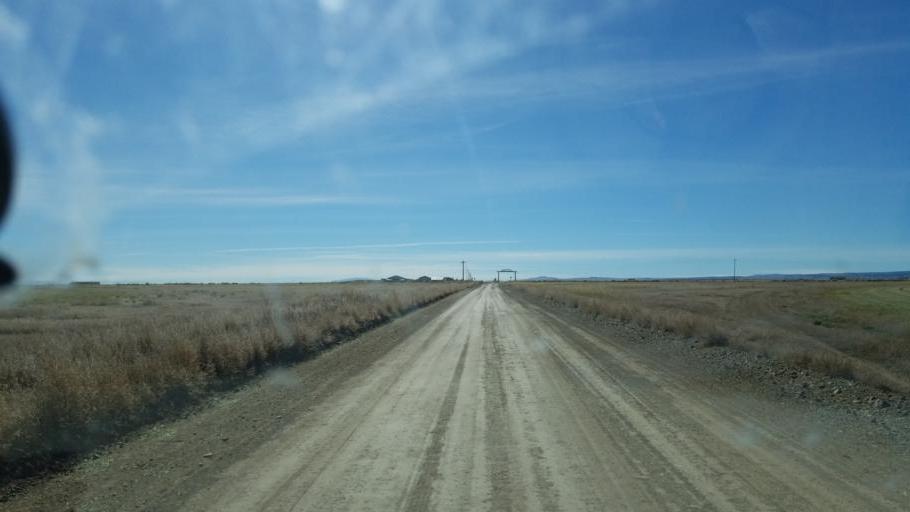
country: US
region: Colorado
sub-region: Rio Grande County
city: Monte Vista
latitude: 37.4040
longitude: -106.1306
